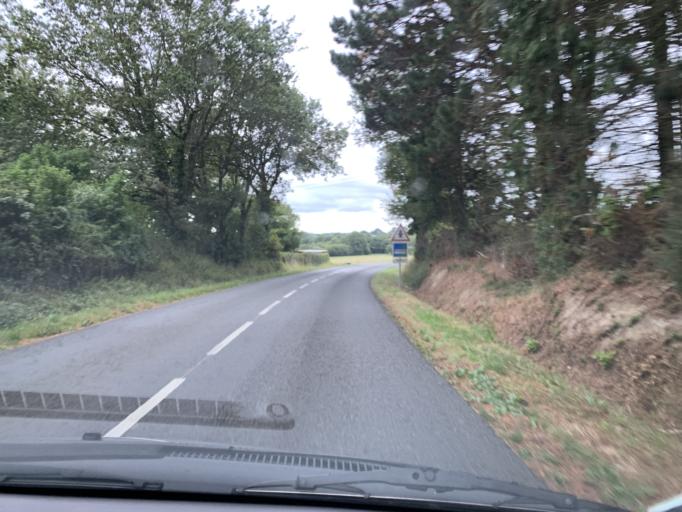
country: FR
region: Pays de la Loire
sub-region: Departement de la Loire-Atlantique
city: Asserac
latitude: 47.4365
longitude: -2.3984
